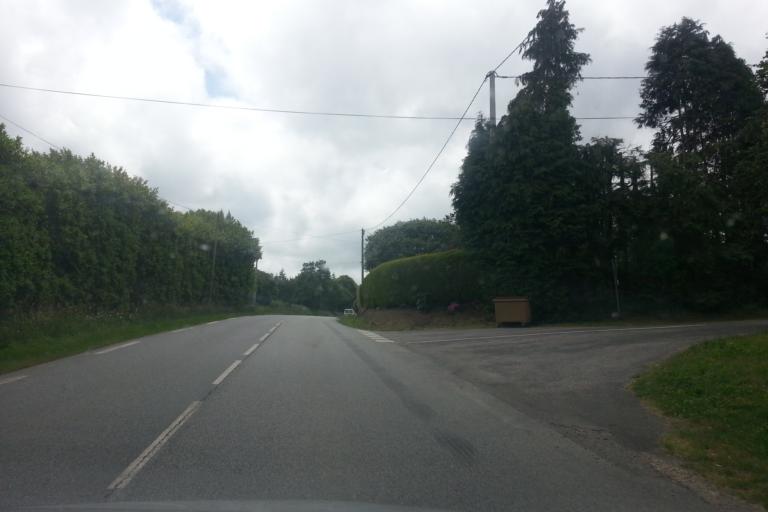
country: FR
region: Brittany
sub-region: Departement du Morbihan
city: Le Faouet
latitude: 48.0578
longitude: -3.4834
